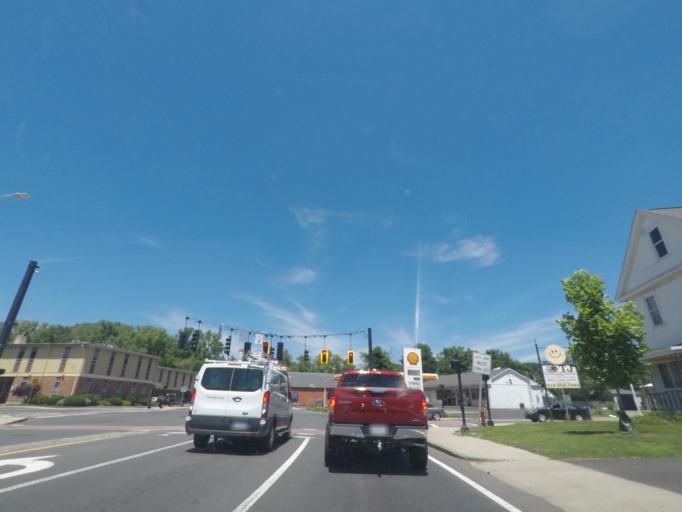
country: US
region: Massachusetts
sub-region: Hampden County
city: Westfield
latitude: 42.1355
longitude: -72.7395
